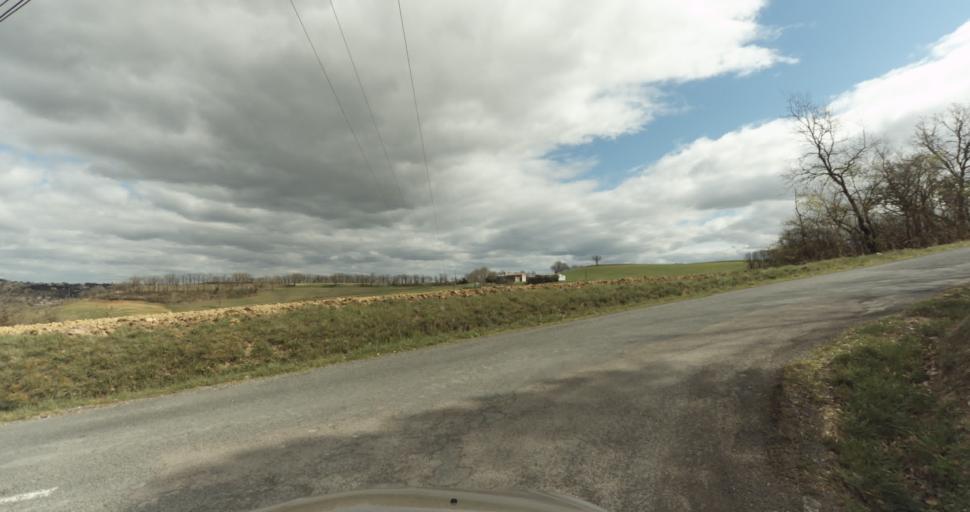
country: FR
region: Midi-Pyrenees
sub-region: Departement du Tarn
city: Puygouzon
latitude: 43.8814
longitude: 2.1551
